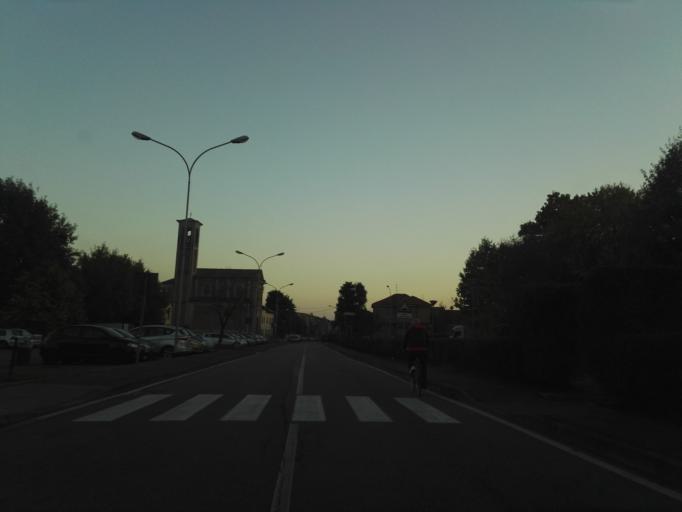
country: IT
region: Lombardy
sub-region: Citta metropolitana di Milano
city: Mezzate
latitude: 45.4477
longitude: 9.2934
